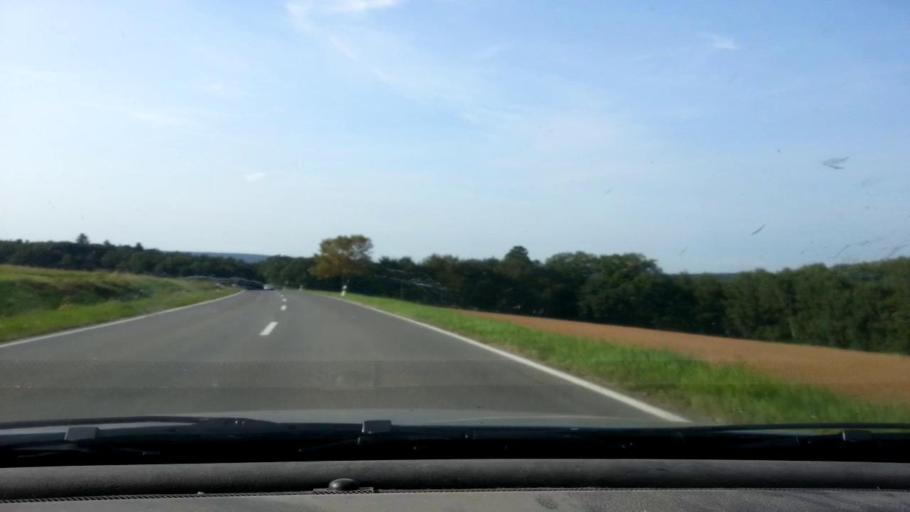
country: DE
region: Bavaria
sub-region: Upper Franconia
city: Zapfendorf
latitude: 50.0061
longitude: 10.9509
